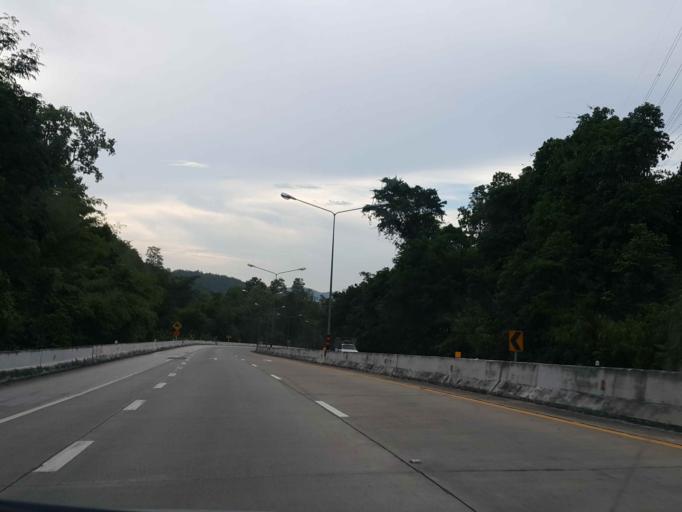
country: TH
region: Lamphun
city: Mae Tha
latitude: 18.4279
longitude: 99.2080
